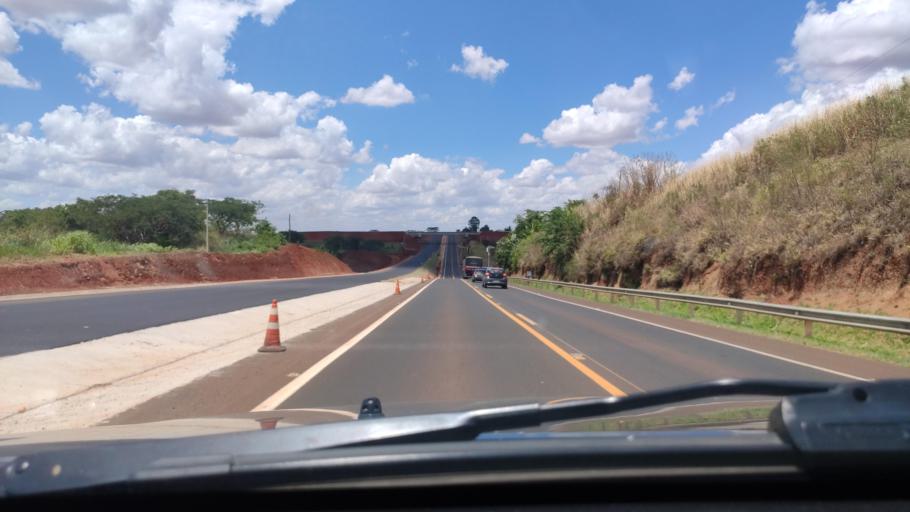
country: BR
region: Sao Paulo
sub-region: Jau
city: Jau
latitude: -22.2142
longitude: -48.5194
